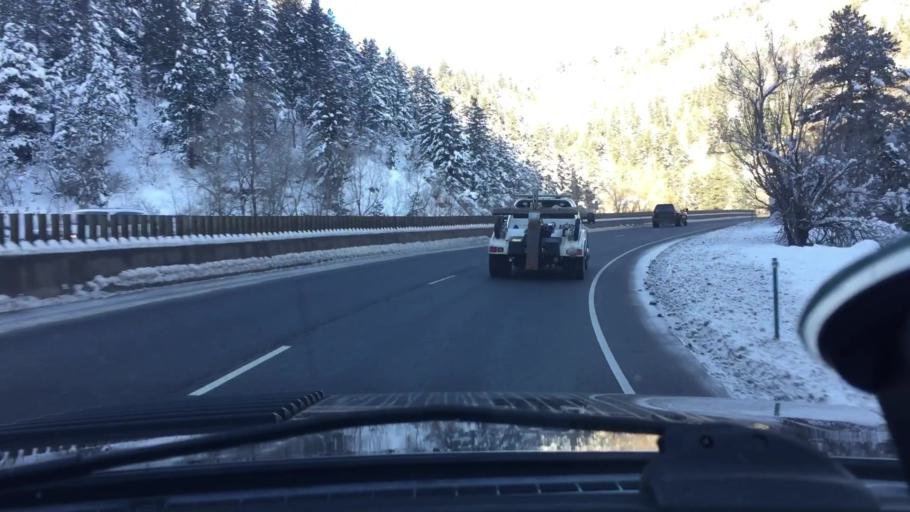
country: US
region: Colorado
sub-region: Jefferson County
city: Indian Hills
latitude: 39.6182
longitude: -105.2247
